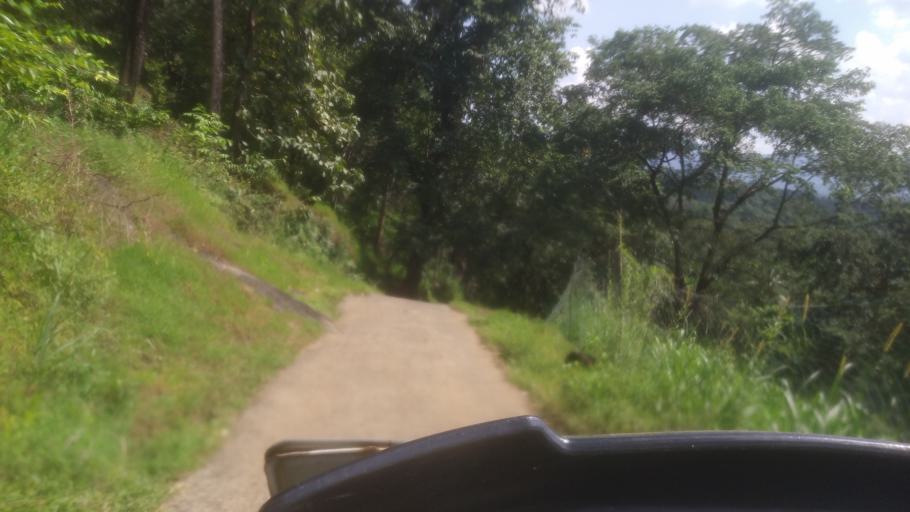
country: IN
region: Kerala
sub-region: Idukki
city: Idukki
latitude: 9.9630
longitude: 76.8245
